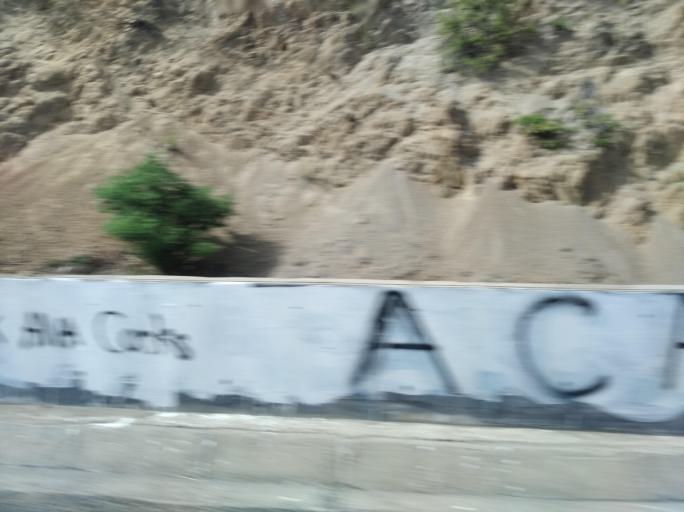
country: CL
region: Valparaiso
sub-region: Provincia de San Felipe
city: Llaillay
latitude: -33.0646
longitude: -71.0178
